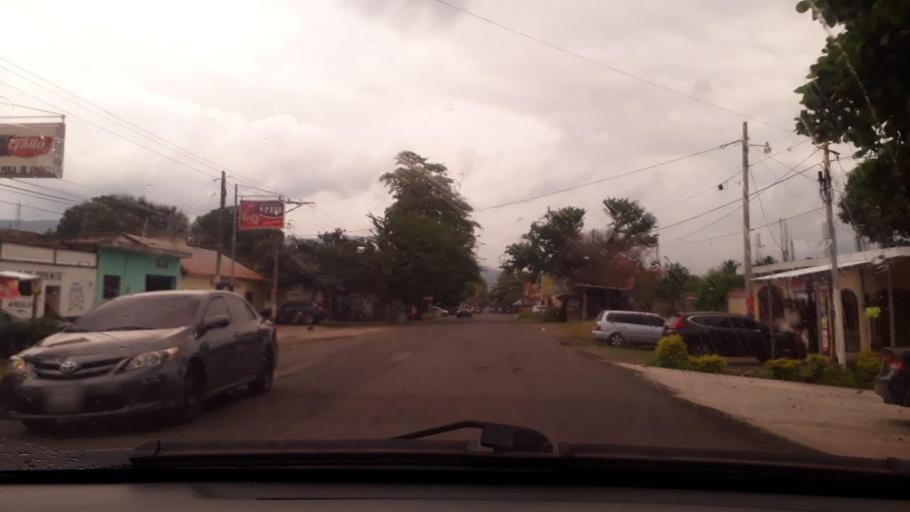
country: GT
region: Jutiapa
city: Jalpatagua
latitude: 14.1374
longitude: -90.0140
